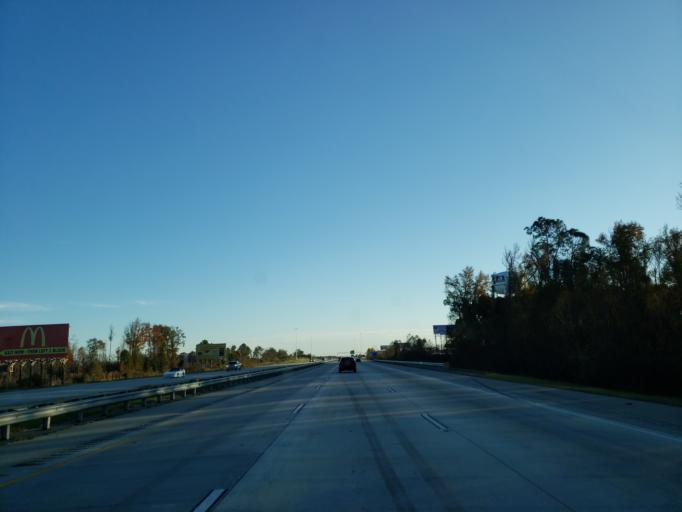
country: US
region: Georgia
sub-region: Dooly County
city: Vienna
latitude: 32.0976
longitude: -83.7632
